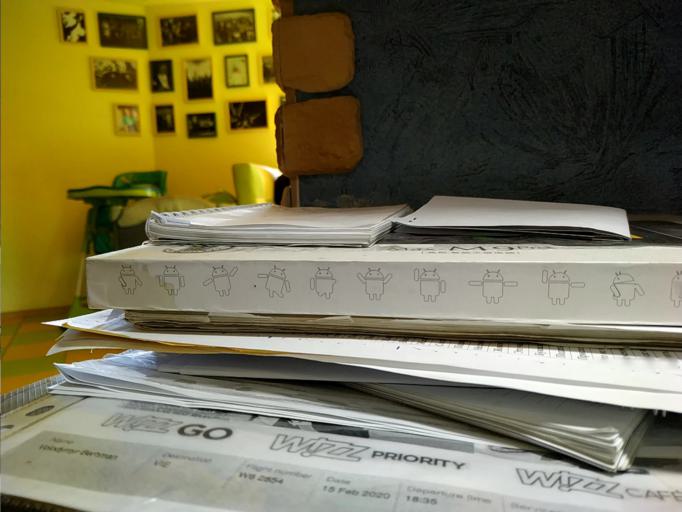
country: RU
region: Pskov
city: Plyussa
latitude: 58.5224
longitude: 29.5229
